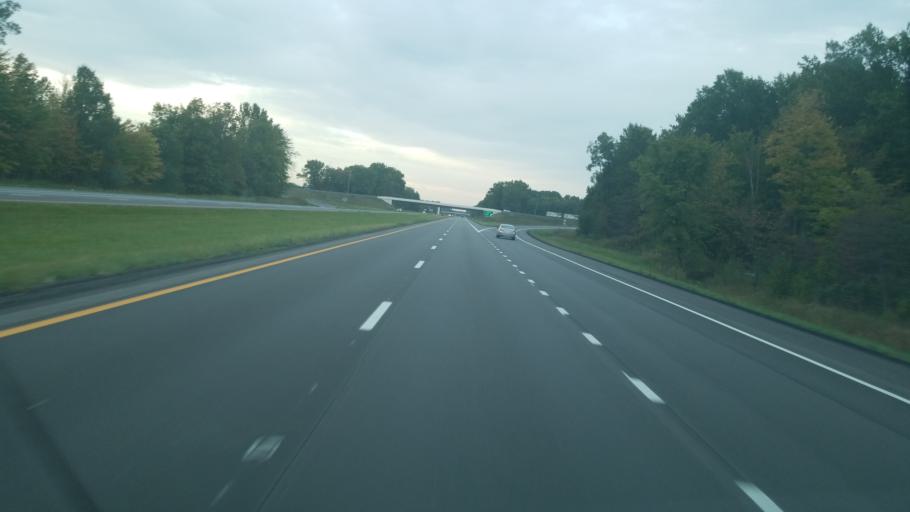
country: US
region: Ohio
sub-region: Trumbull County
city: Cortland
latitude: 41.3073
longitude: -80.7049
